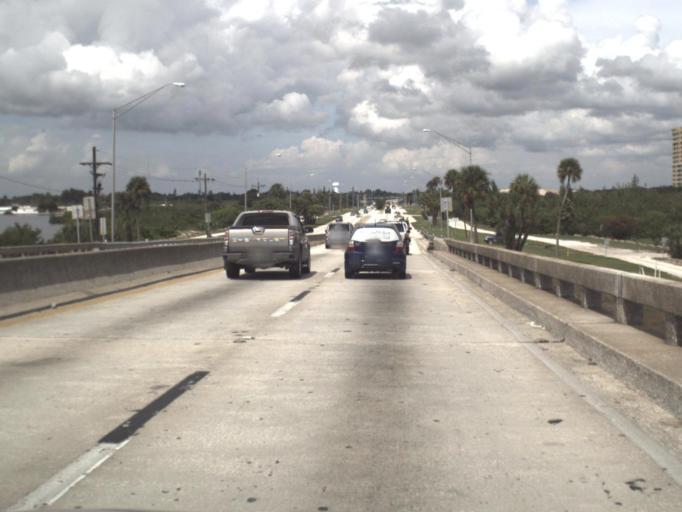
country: US
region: Florida
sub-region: Manatee County
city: Bradenton
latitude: 27.5061
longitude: -82.5630
